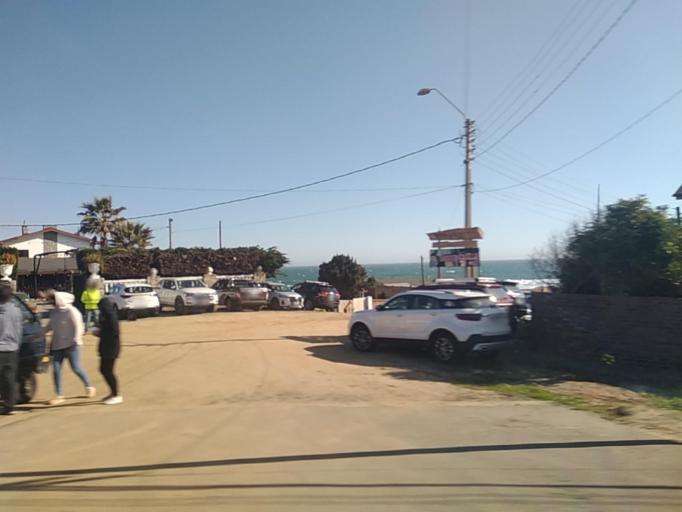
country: CL
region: Valparaiso
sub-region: San Antonio Province
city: El Tabo
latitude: -33.4544
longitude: -71.6718
